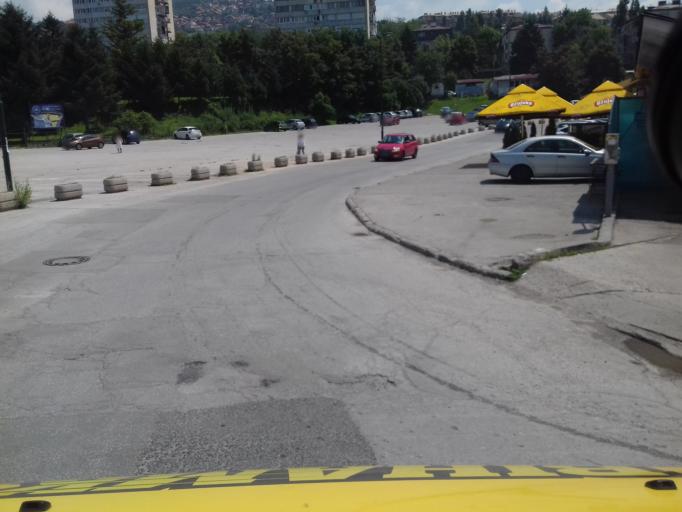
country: BA
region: Federation of Bosnia and Herzegovina
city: Kobilja Glava
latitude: 43.8729
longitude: 18.4101
